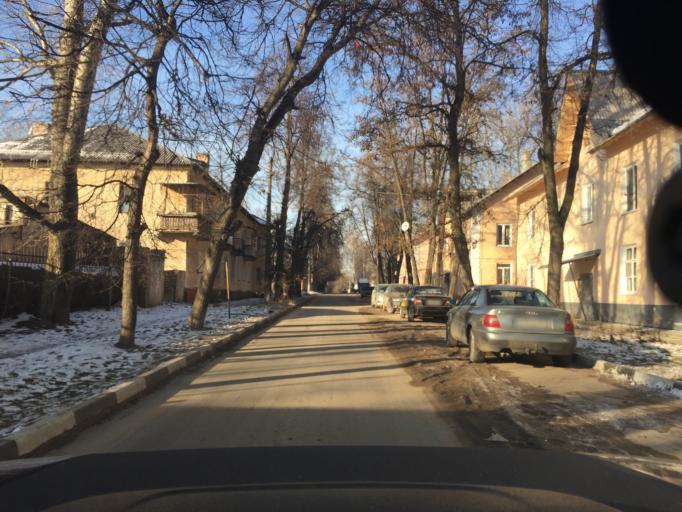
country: RU
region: Tula
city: Tula
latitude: 54.1802
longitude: 37.7087
